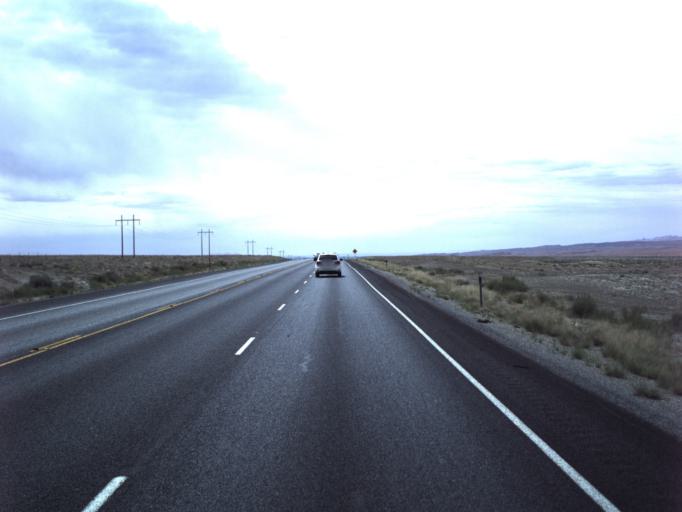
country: US
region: Utah
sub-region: Carbon County
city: East Carbon City
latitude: 39.1878
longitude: -110.3385
